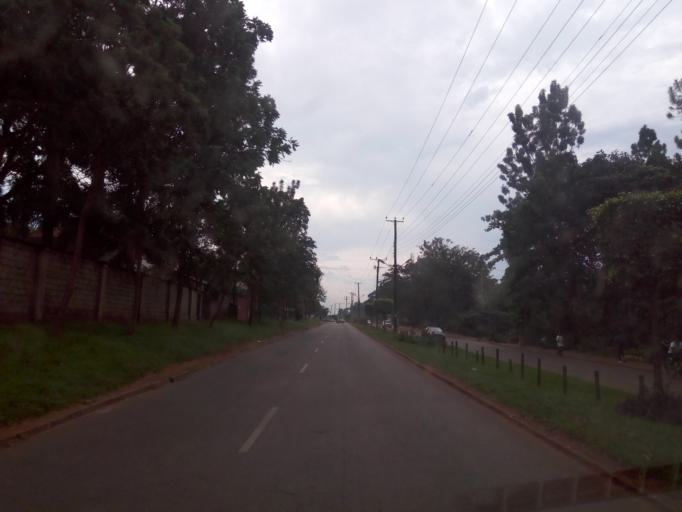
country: UG
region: Central Region
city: Kampala Central Division
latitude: 0.3304
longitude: 32.5813
